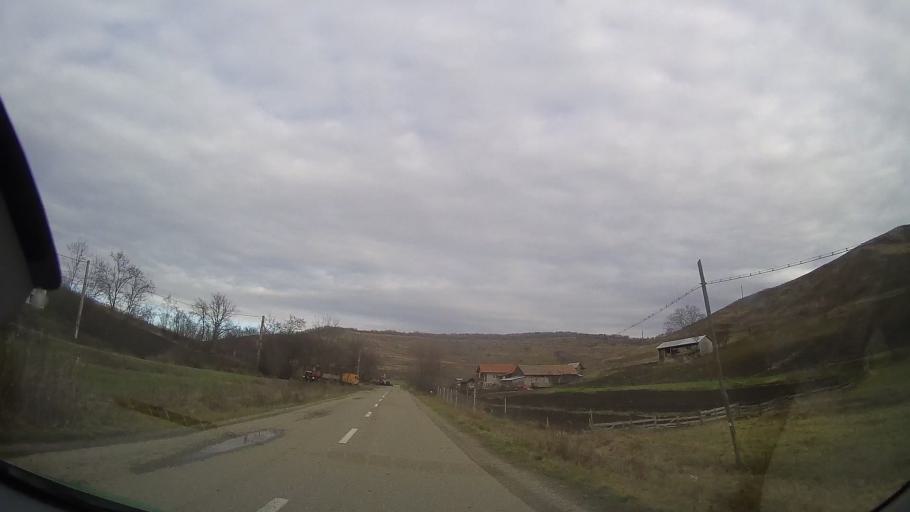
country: RO
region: Bistrita-Nasaud
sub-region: Comuna Micestii de Campie
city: Micestii de Campie
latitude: 46.8358
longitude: 24.3031
